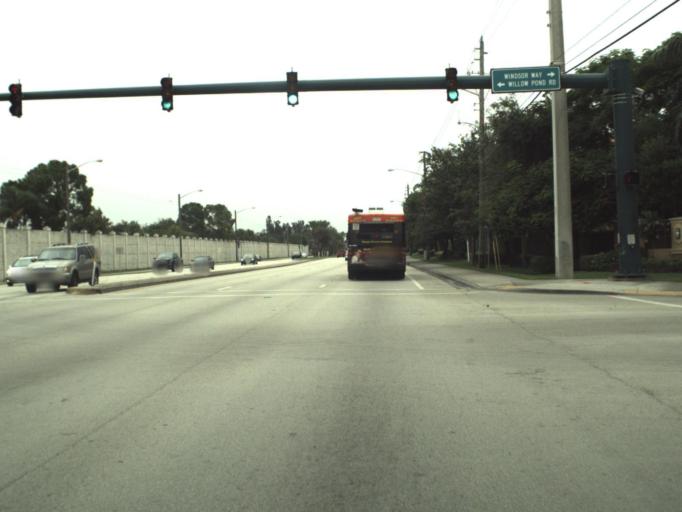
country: US
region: Florida
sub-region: Palm Beach County
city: Schall Circle
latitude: 26.7410
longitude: -80.1095
